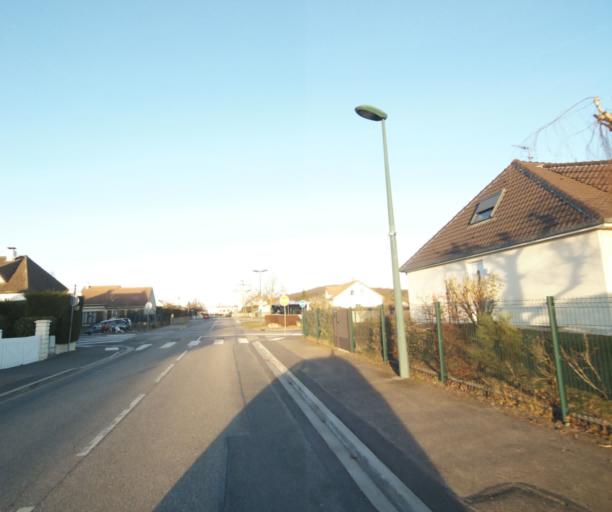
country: FR
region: Lorraine
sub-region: Departement de Meurthe-et-Moselle
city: Saulxures-les-Nancy
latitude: 48.6904
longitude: 6.2464
